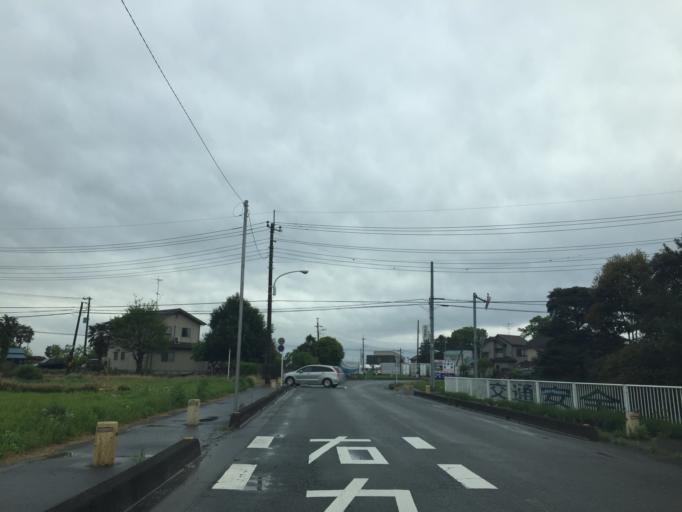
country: JP
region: Saitama
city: Shiki
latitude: 35.8642
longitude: 139.5695
